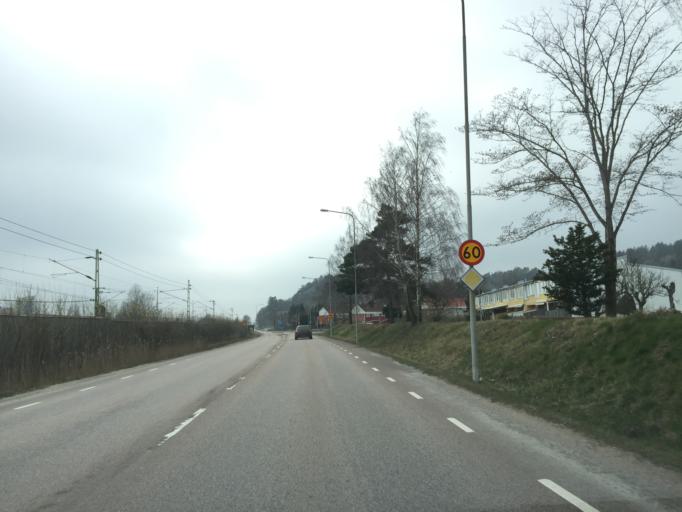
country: SE
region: Vaestra Goetaland
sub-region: Partille Kommun
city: Partille
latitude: 57.7440
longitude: 12.1161
